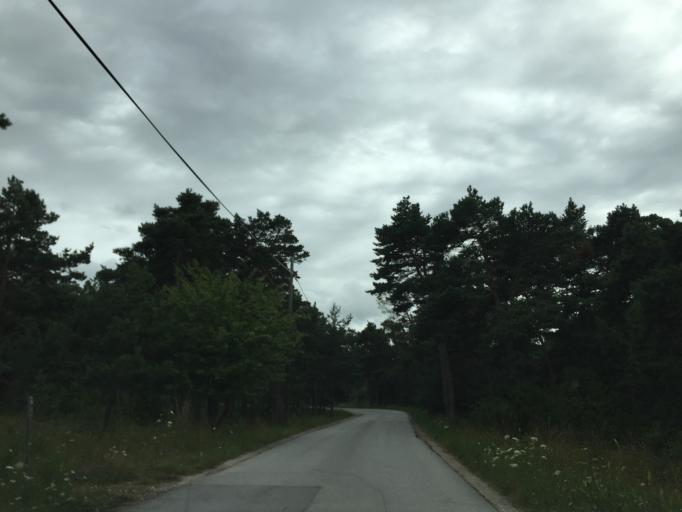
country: SE
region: Gotland
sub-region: Gotland
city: Visby
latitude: 57.7049
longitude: 18.3764
